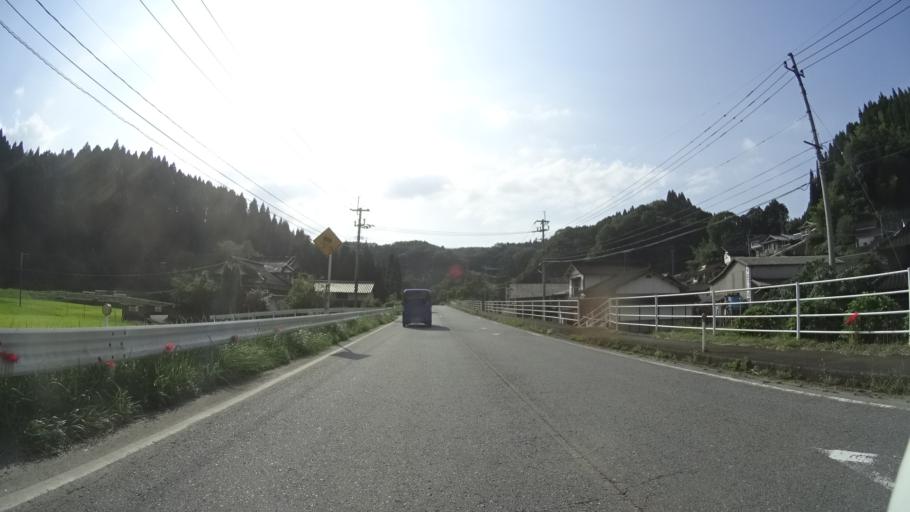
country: JP
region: Kumamoto
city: Aso
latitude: 32.6854
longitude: 131.0474
